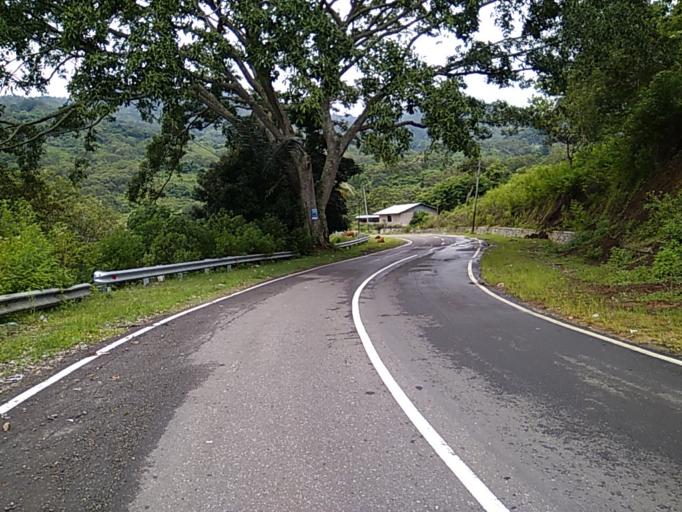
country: ID
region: East Nusa Tenggara
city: Koanara
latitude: -8.7500
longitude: 121.8476
